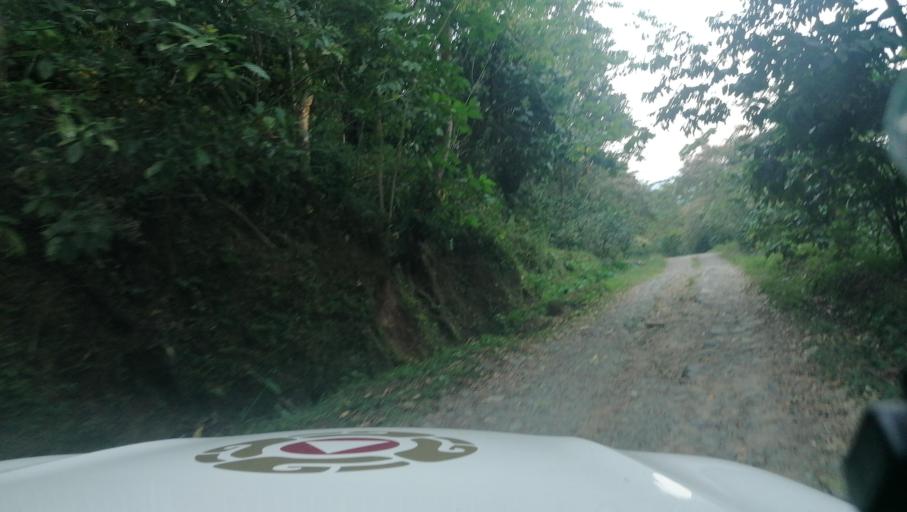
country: MX
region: Chiapas
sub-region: Cacahoatan
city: Benito Juarez
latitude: 15.0979
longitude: -92.2195
